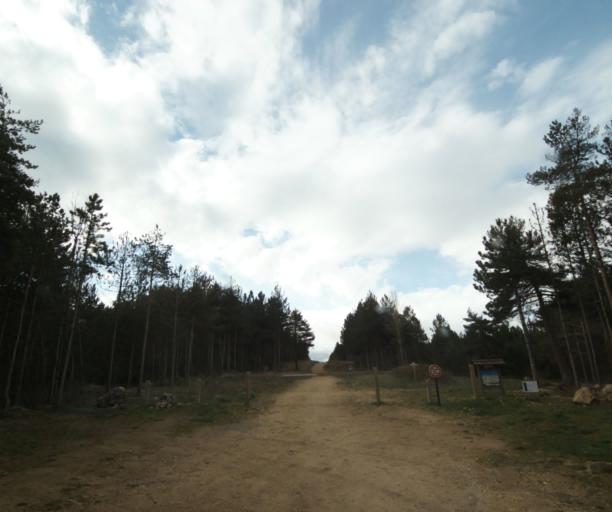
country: FR
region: Midi-Pyrenees
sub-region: Departement de l'Aveyron
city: Millau
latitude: 44.1259
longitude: 3.1529
